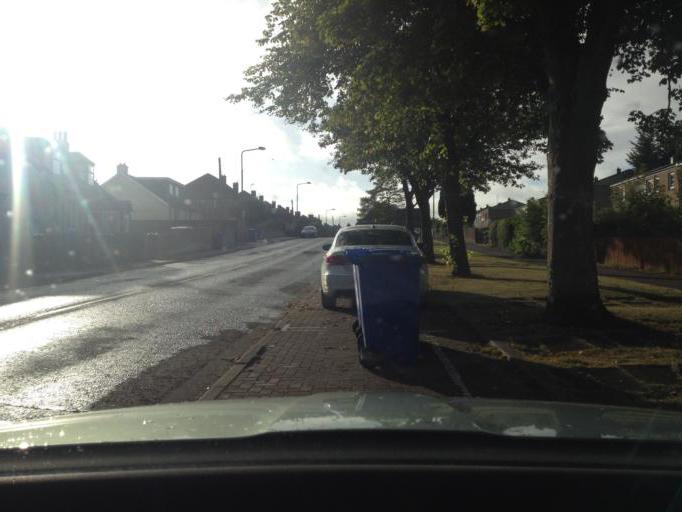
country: GB
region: Scotland
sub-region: West Lothian
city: East Calder
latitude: 55.8932
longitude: -3.4655
